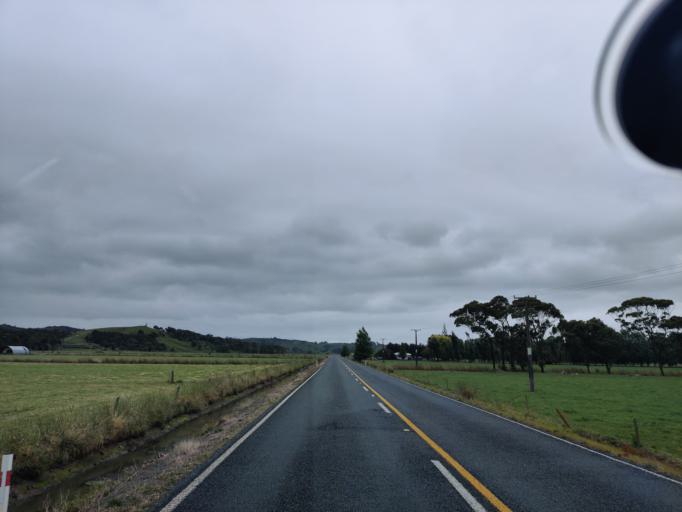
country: NZ
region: Northland
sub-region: Kaipara District
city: Dargaville
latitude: -36.1192
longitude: 174.0765
